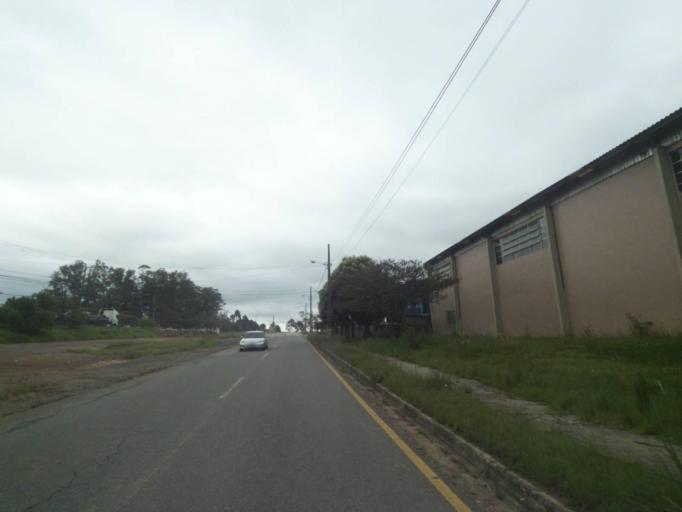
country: BR
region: Parana
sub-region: Araucaria
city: Araucaria
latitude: -25.5454
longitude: -49.3146
